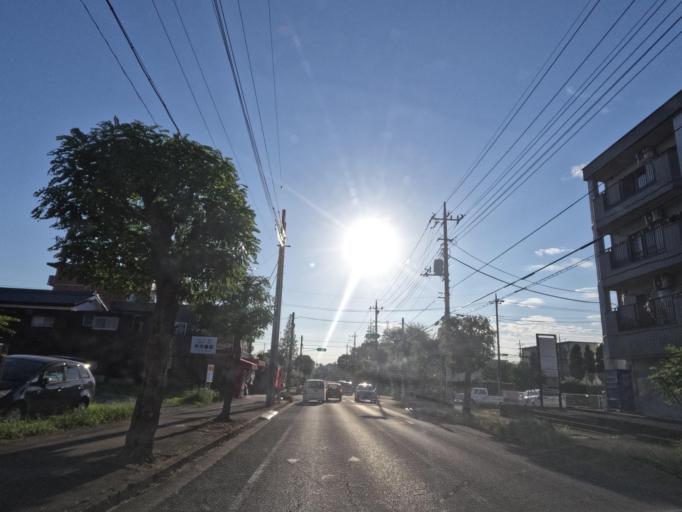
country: JP
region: Ibaraki
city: Moriya
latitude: 35.9247
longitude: 140.0146
